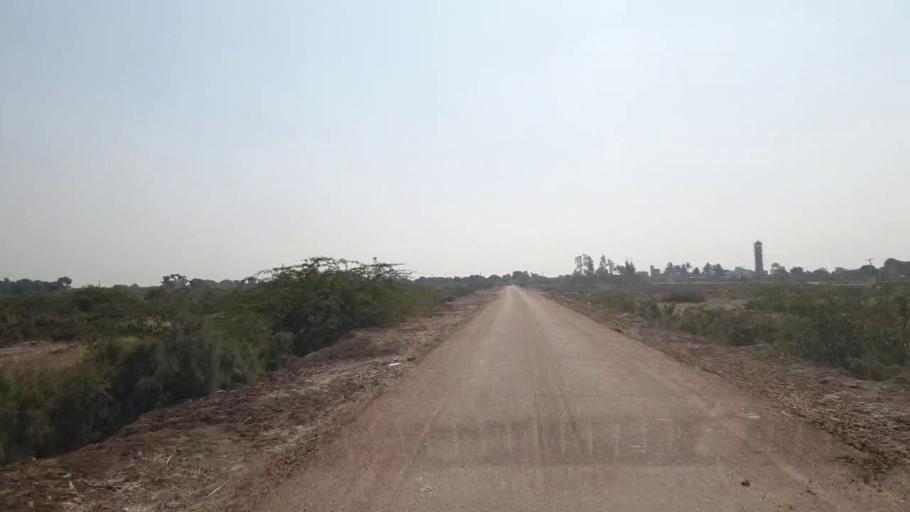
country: PK
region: Sindh
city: Chambar
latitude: 25.3792
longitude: 68.8808
